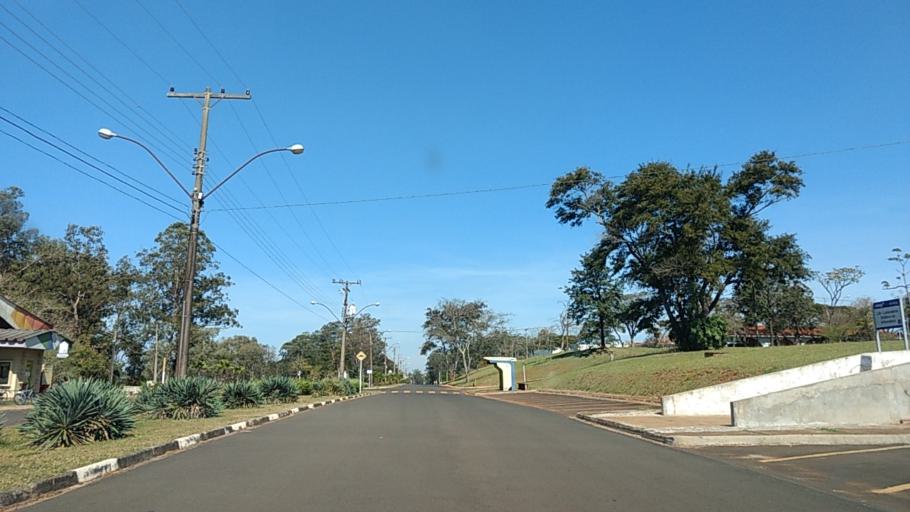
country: BR
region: Sao Paulo
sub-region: Botucatu
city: Botucatu
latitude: -22.8483
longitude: -48.4341
